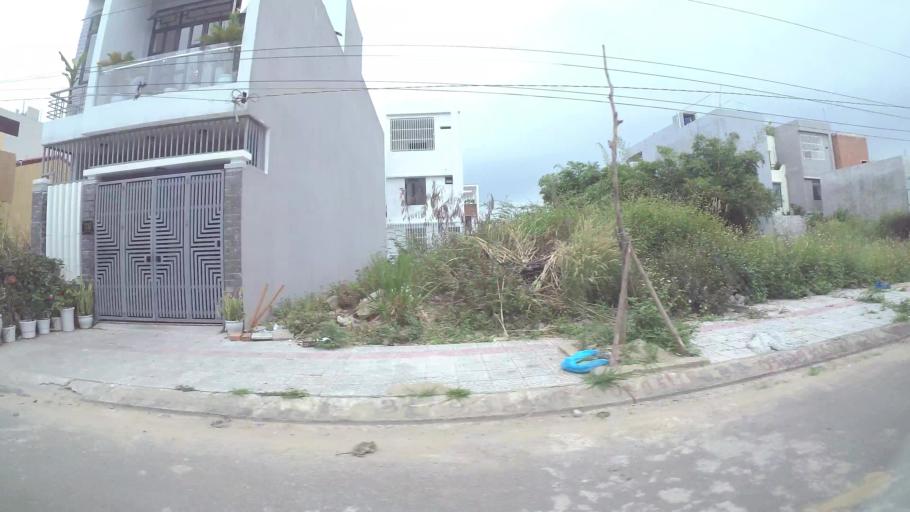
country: VN
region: Da Nang
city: Lien Chieu
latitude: 16.0719
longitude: 108.1645
